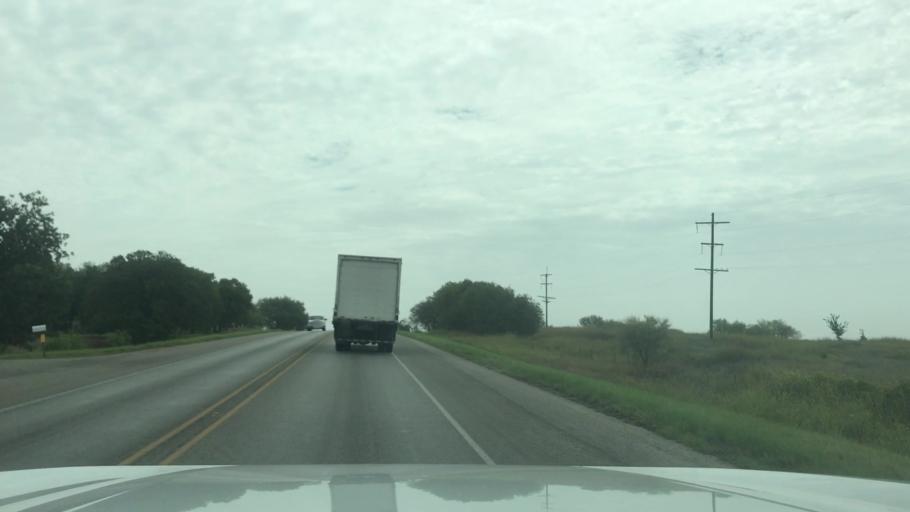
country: US
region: Texas
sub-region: Comanche County
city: De Leon
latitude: 32.1009
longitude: -98.4754
